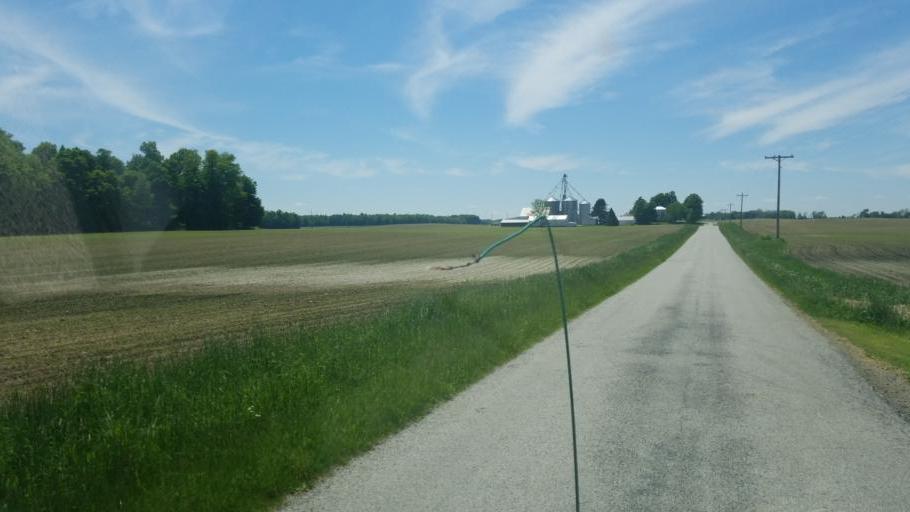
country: US
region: Ohio
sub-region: Huron County
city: Willard
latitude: 41.1226
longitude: -82.6307
